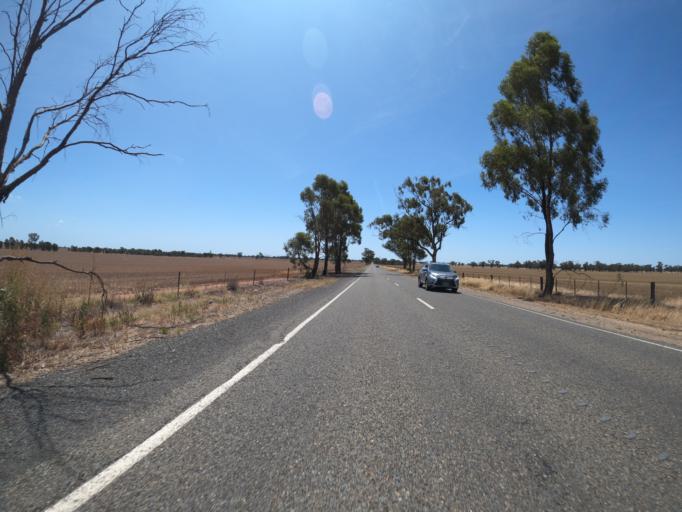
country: AU
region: Victoria
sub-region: Moira
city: Yarrawonga
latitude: -36.0774
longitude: 145.9954
